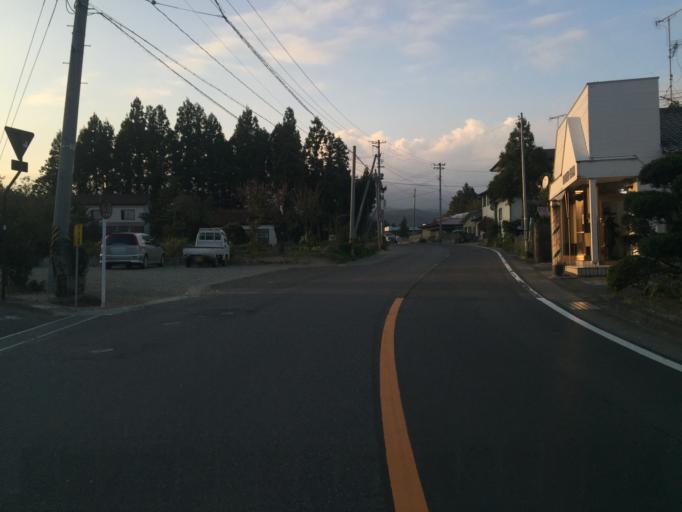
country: JP
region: Fukushima
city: Motomiya
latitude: 37.5547
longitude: 140.3575
